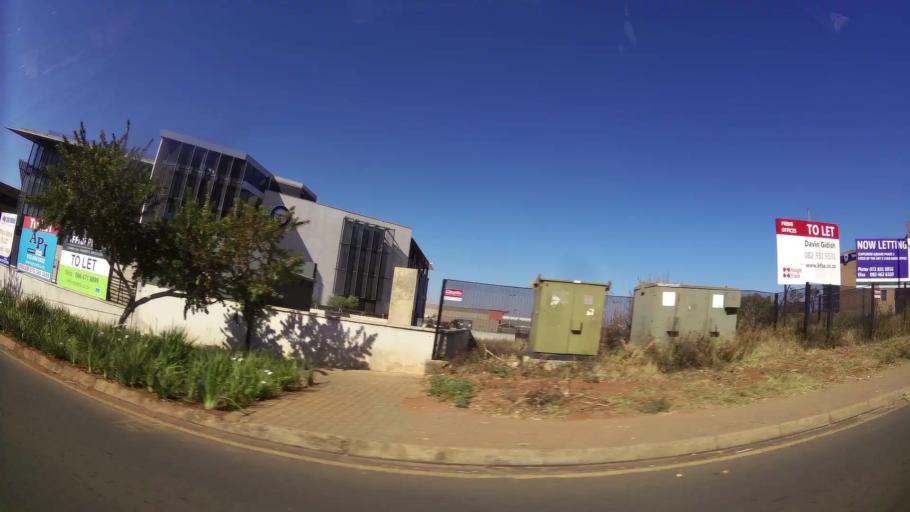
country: ZA
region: Gauteng
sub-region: City of Tshwane Metropolitan Municipality
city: Centurion
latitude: -25.8565
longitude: 28.1833
